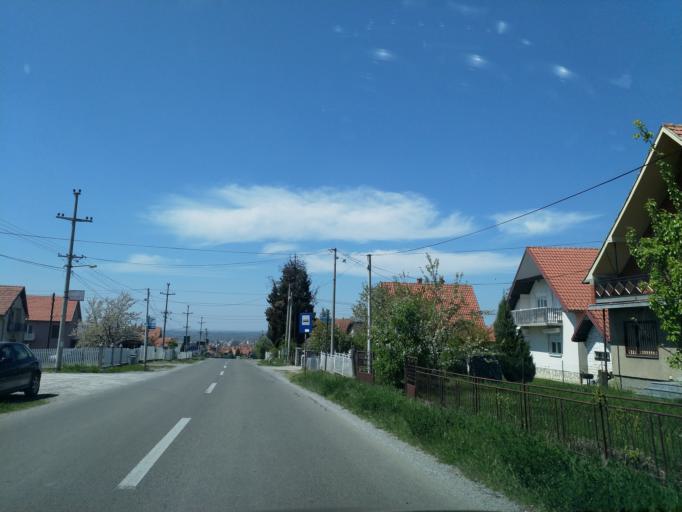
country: RS
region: Central Serbia
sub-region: Belgrade
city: Lazarevac
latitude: 44.3748
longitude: 20.2947
